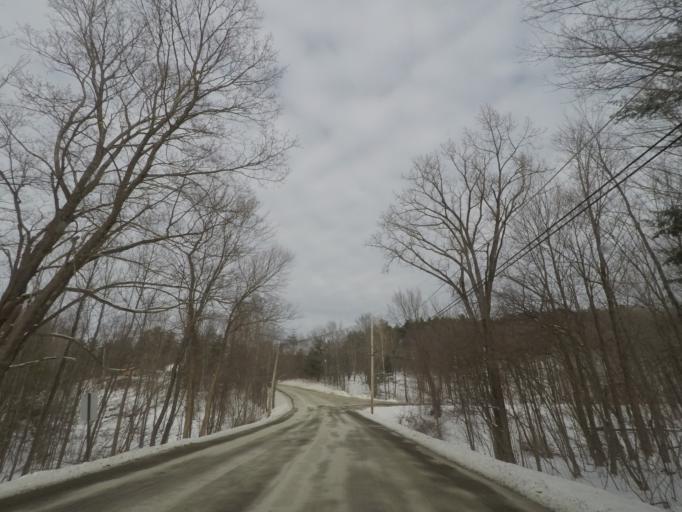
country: US
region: New York
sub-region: Rensselaer County
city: Averill Park
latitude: 42.6154
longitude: -73.5415
